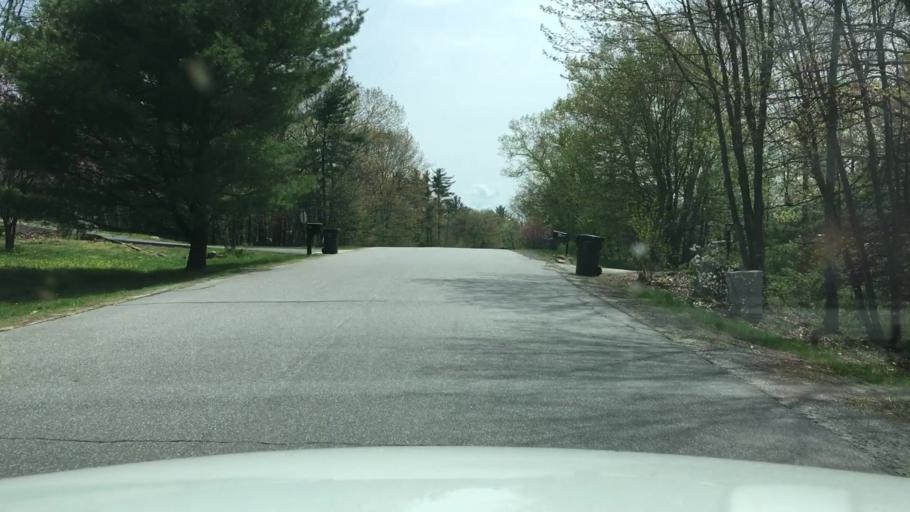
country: US
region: New Hampshire
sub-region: Rockingham County
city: Londonderry
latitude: 42.8314
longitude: -71.3732
